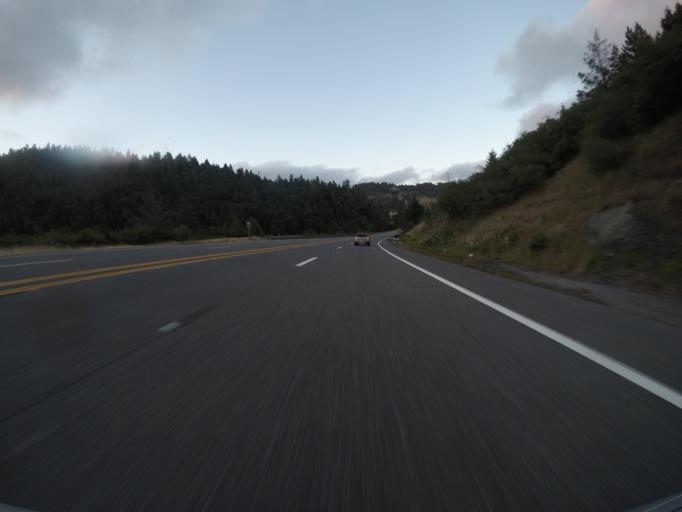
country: US
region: California
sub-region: Humboldt County
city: Redway
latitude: 40.0559
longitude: -123.7911
